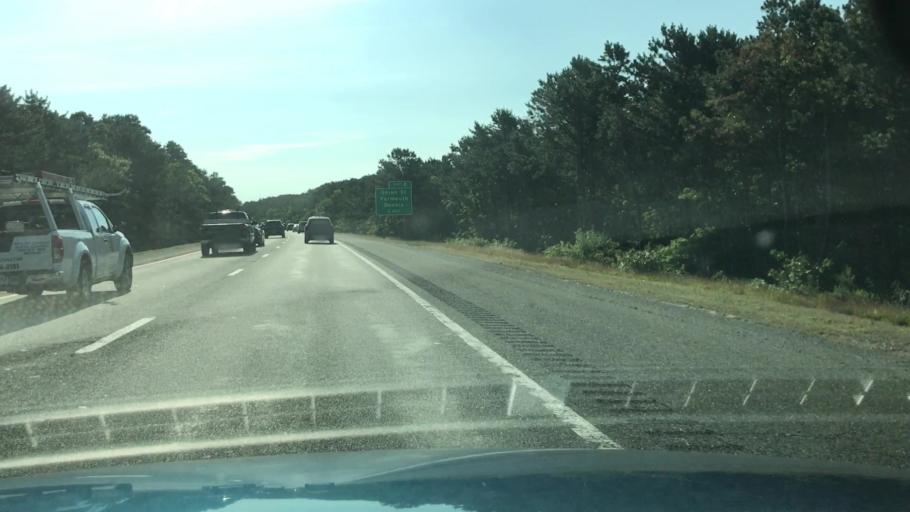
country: US
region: Massachusetts
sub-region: Barnstable County
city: Yarmouth Port
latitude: 41.6856
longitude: -70.2425
